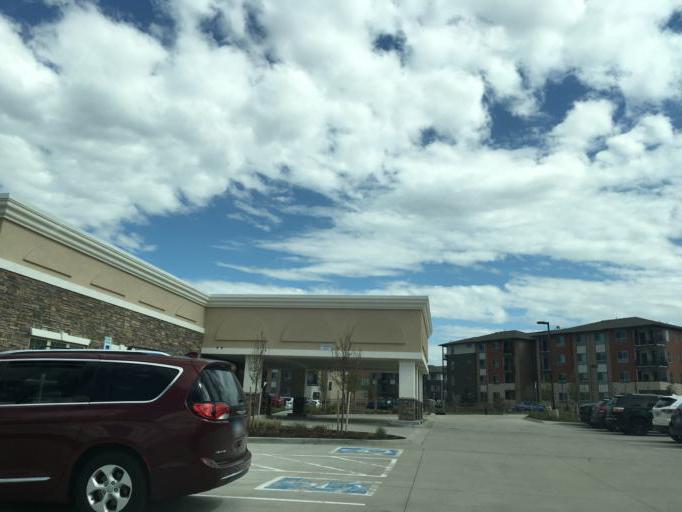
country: US
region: Colorado
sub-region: Jefferson County
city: West Pleasant View
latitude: 39.7272
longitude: -105.2052
